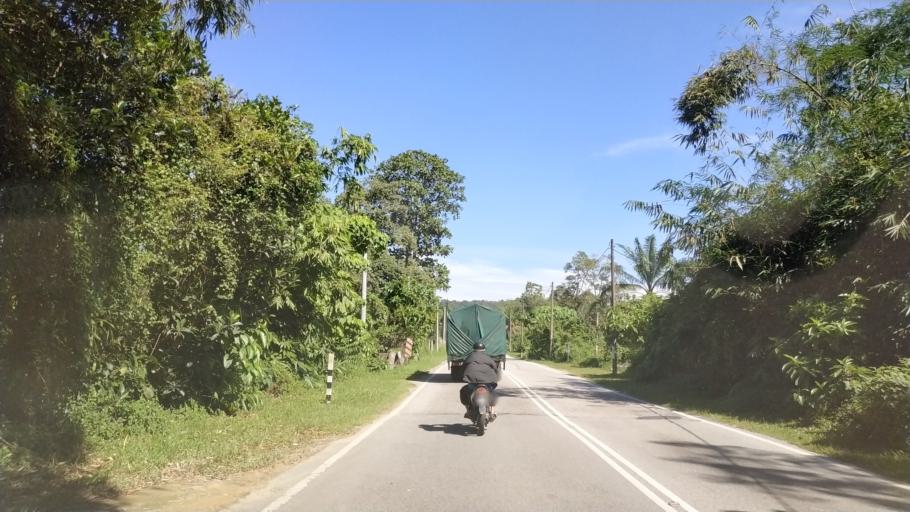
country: MY
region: Kedah
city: Kulim
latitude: 5.3113
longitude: 100.5402
